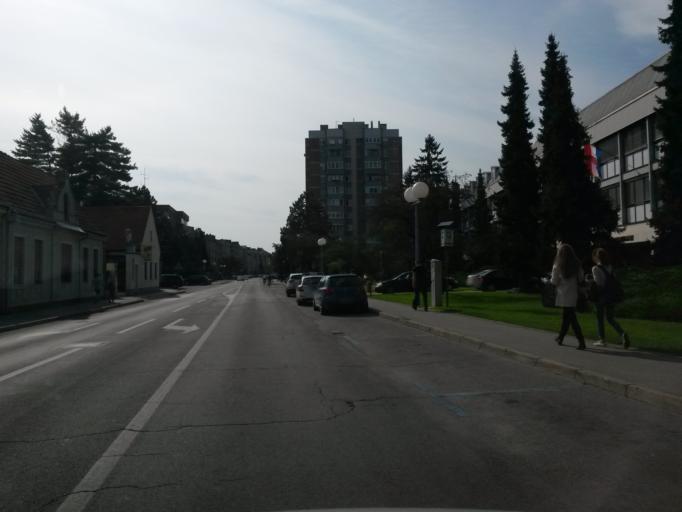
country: HR
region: Varazdinska
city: Varazdin
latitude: 46.3064
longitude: 16.3334
